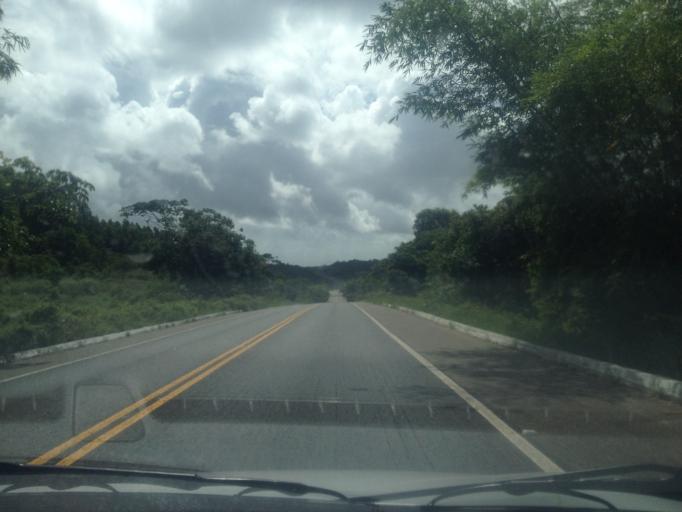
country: BR
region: Bahia
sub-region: Entre Rios
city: Entre Rios
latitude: -12.2059
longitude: -37.8261
